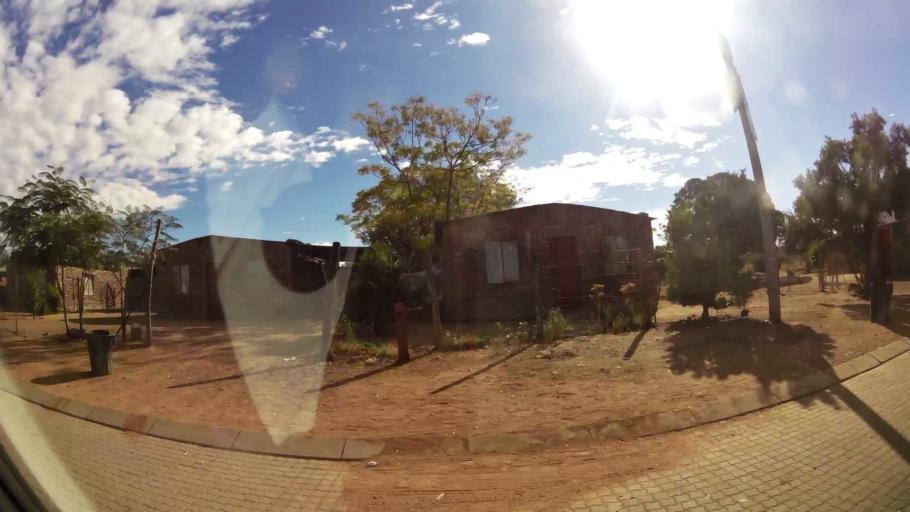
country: ZA
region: Limpopo
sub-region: Waterberg District Municipality
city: Warmbaths
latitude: -24.8787
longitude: 28.2724
